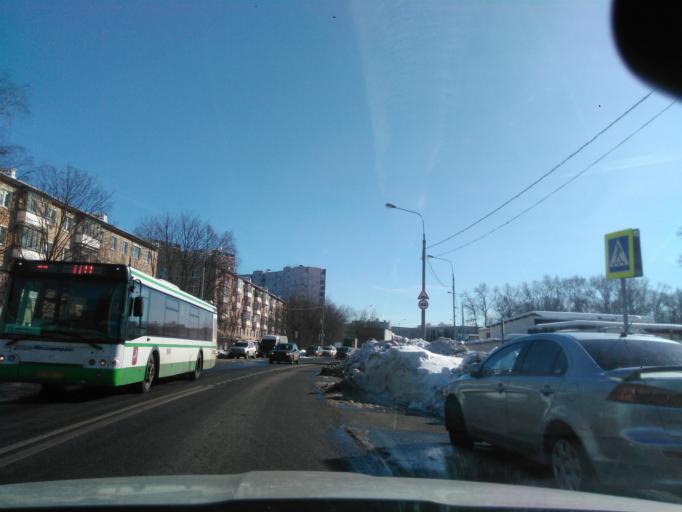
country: RU
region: Moscow
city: Zelenograd
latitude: 55.9871
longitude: 37.1705
